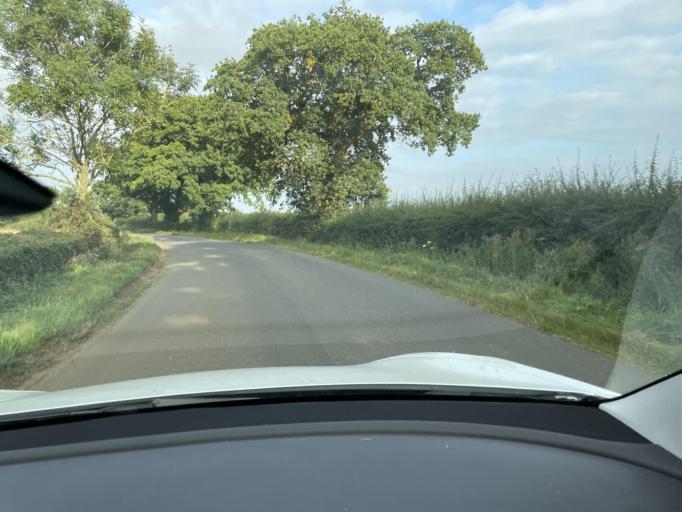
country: GB
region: England
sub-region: Northamptonshire
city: Brixworth
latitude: 52.3939
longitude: -0.9438
